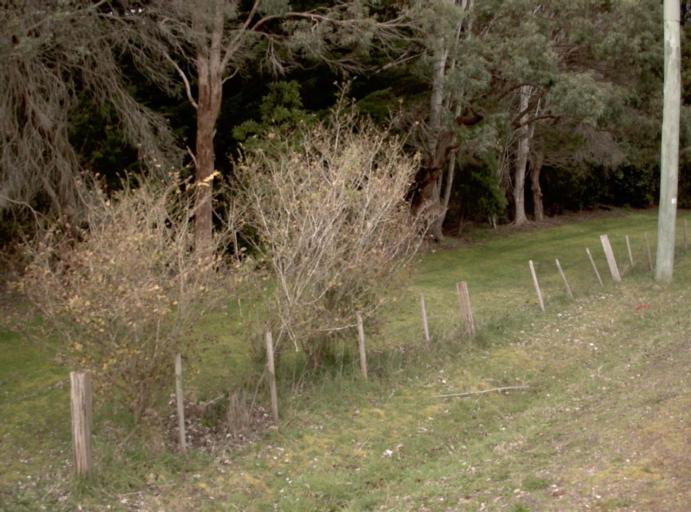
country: AU
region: Tasmania
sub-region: Launceston
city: Mayfield
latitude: -41.2617
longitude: 147.1592
